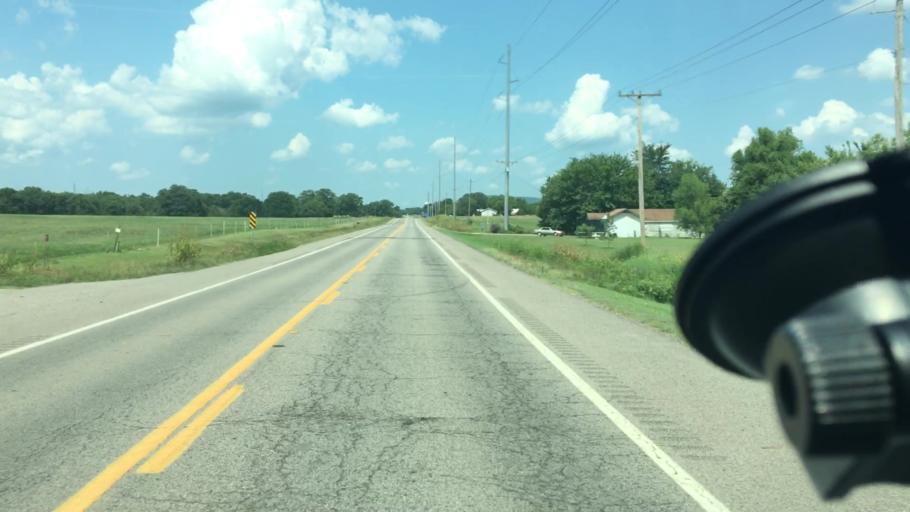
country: US
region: Arkansas
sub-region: Logan County
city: Paris
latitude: 35.2949
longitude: -93.6690
